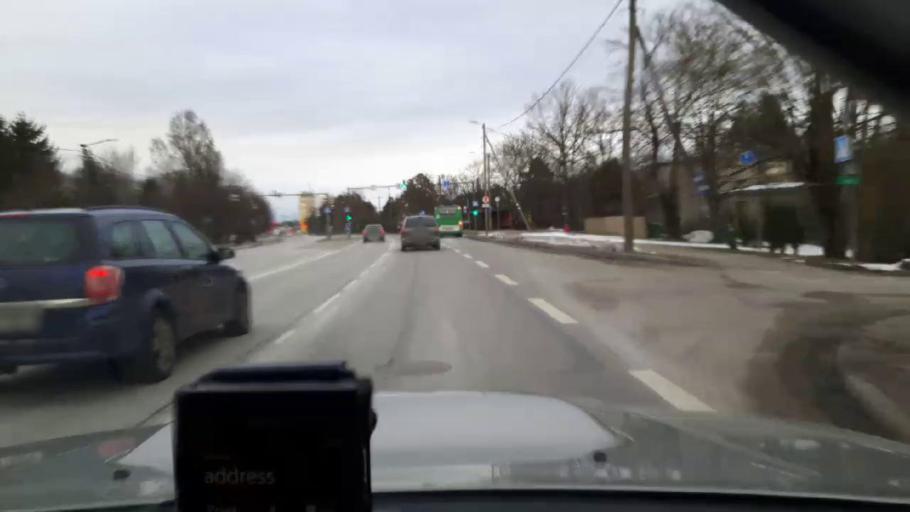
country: EE
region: Harju
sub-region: Saue vald
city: Laagri
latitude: 59.3553
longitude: 24.6309
